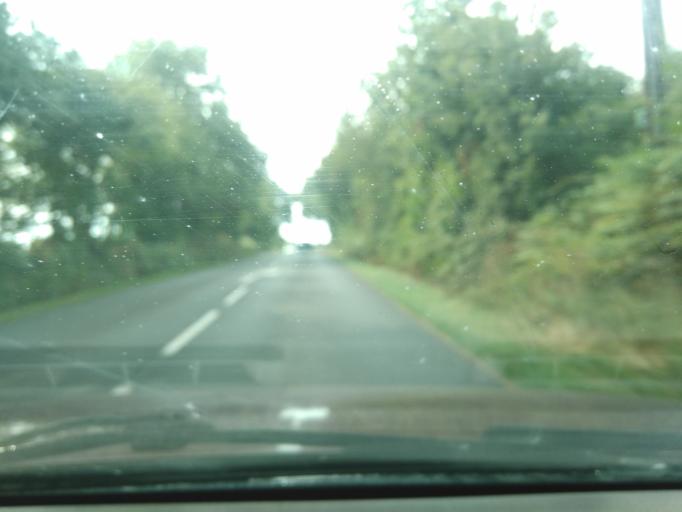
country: FR
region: Pays de la Loire
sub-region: Departement de la Vendee
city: Dompierre-sur-Yon
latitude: 46.7333
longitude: -1.3752
